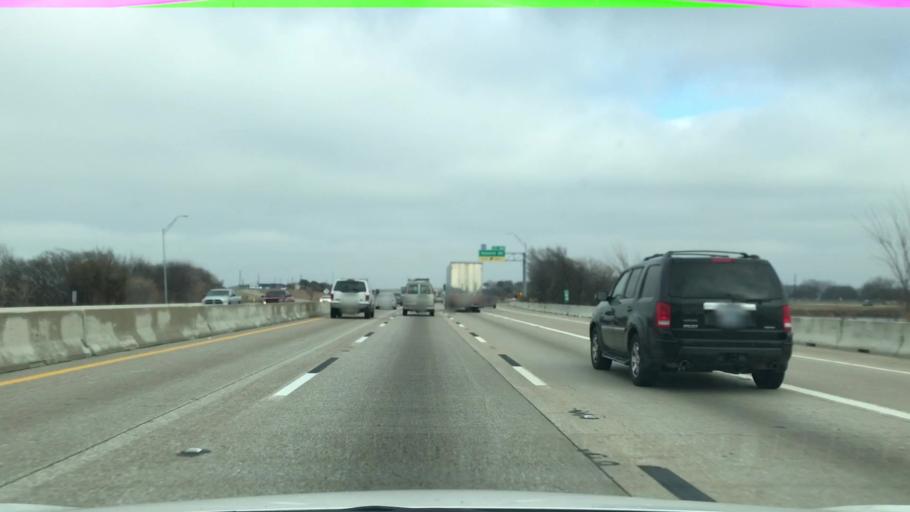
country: US
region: Texas
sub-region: Dallas County
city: Rowlett
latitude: 32.8735
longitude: -96.5248
